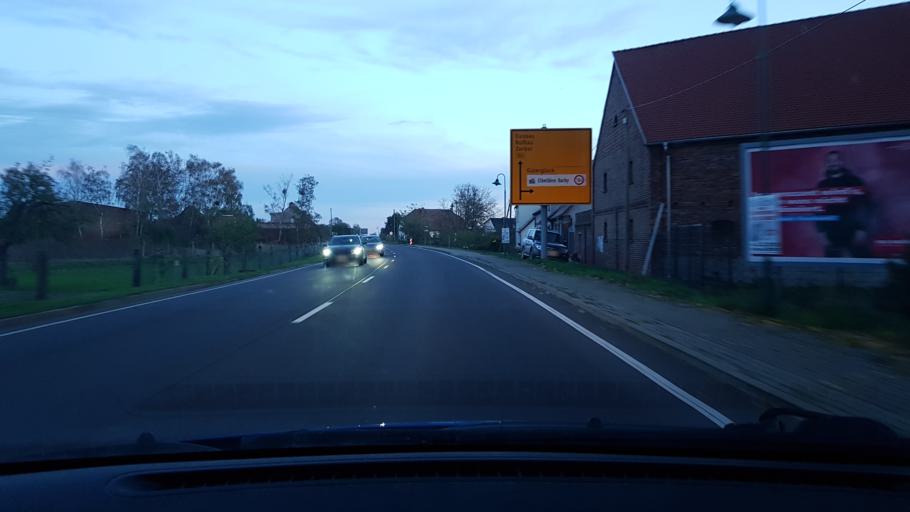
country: DE
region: Saxony-Anhalt
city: Leitzkau
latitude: 52.0156
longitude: 12.0124
